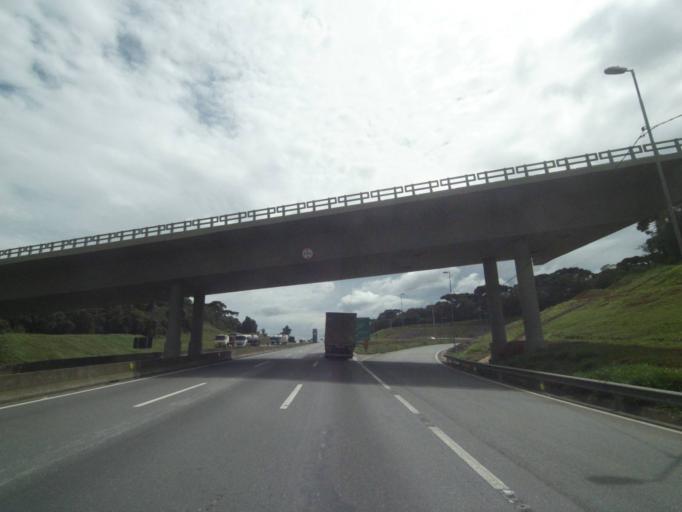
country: BR
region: Parana
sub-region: Sao Jose Dos Pinhais
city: Sao Jose dos Pinhais
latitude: -25.5204
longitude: -49.1346
